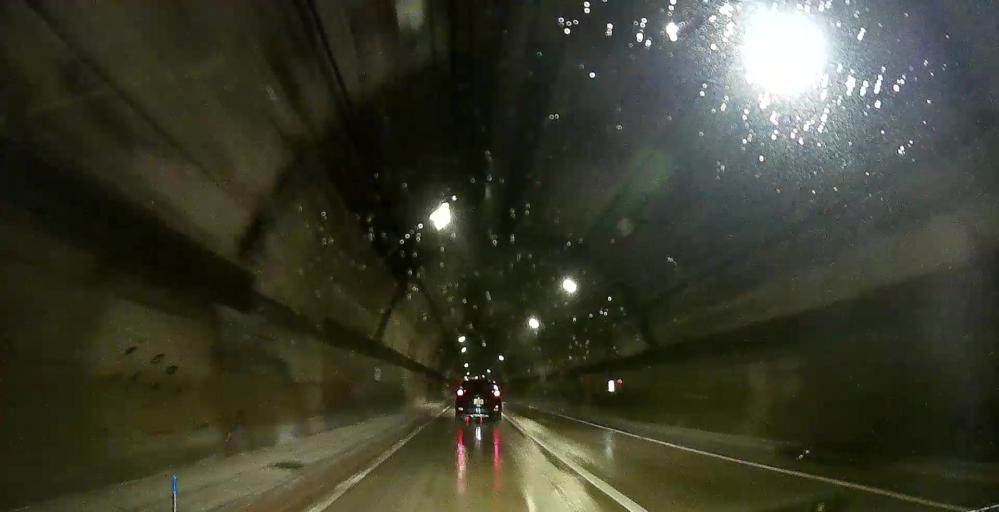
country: JP
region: Yamagata
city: Nagai
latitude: 38.0475
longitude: 139.7874
